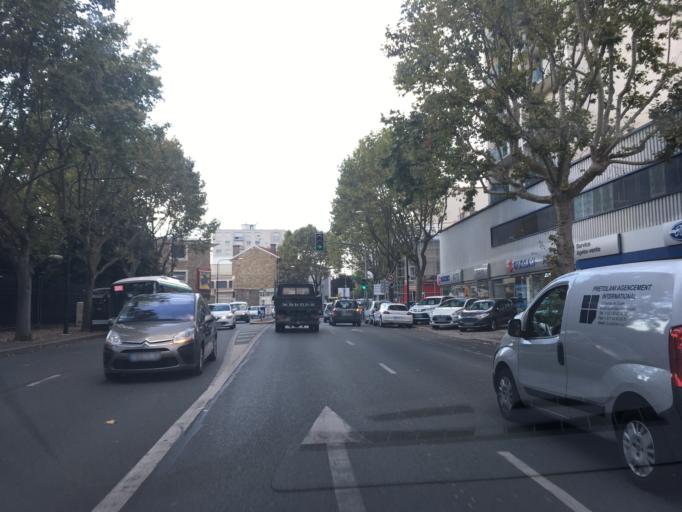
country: FR
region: Ile-de-France
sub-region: Departement du Val-de-Marne
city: Joinville-le-Pont
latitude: 48.8106
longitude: 2.4701
